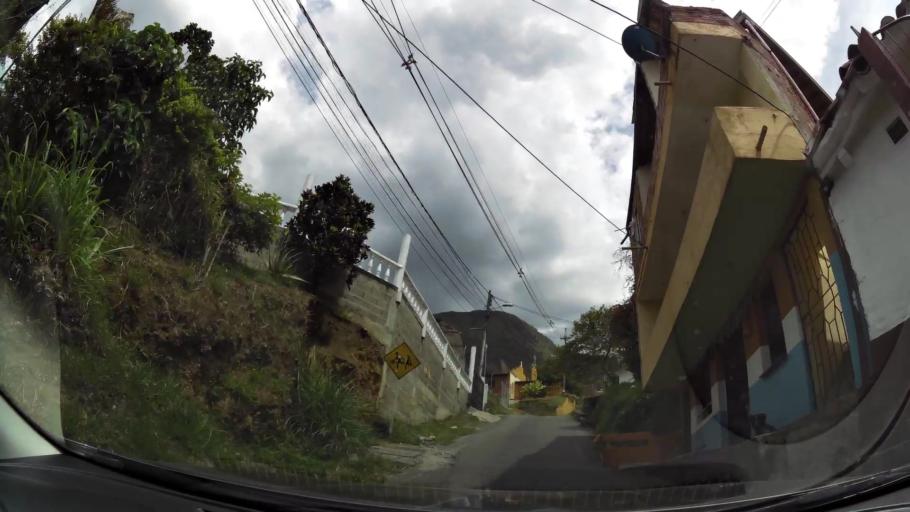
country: CO
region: Antioquia
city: Municipio de Copacabana
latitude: 6.3271
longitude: -75.5004
